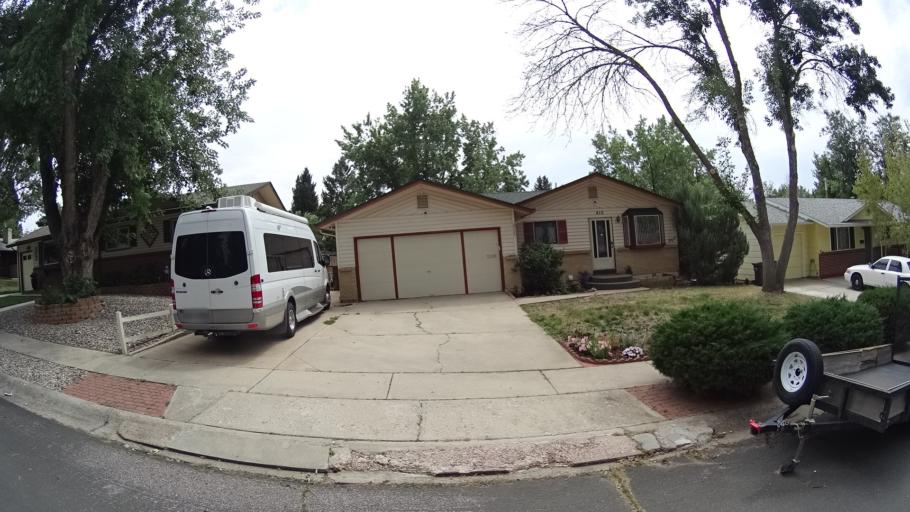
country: US
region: Colorado
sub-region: El Paso County
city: Colorado Springs
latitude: 38.8936
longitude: -104.8108
